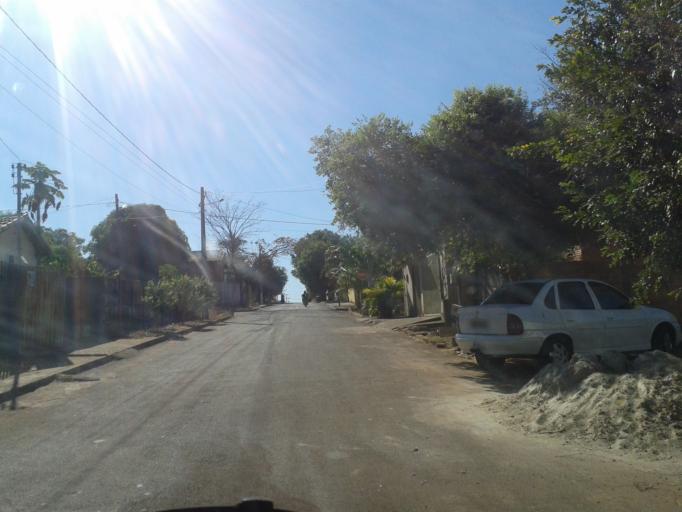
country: BR
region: Goias
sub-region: Sao Miguel Do Araguaia
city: Sao Miguel do Araguaia
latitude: -13.2794
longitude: -50.1562
